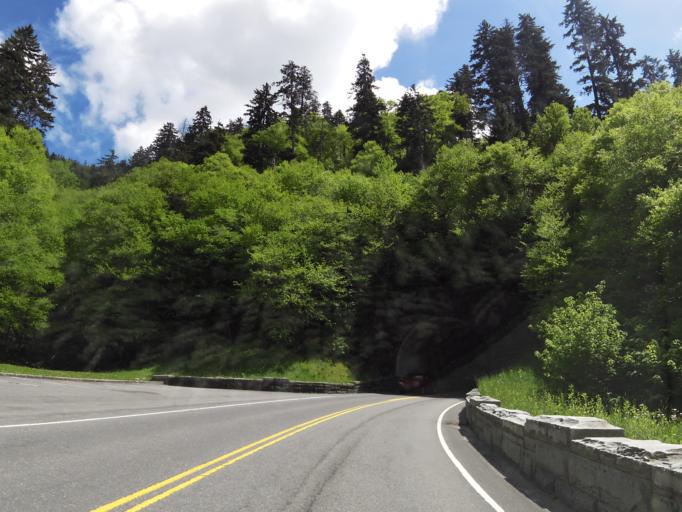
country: US
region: Tennessee
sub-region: Sevier County
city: Gatlinburg
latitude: 35.6179
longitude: -83.4193
